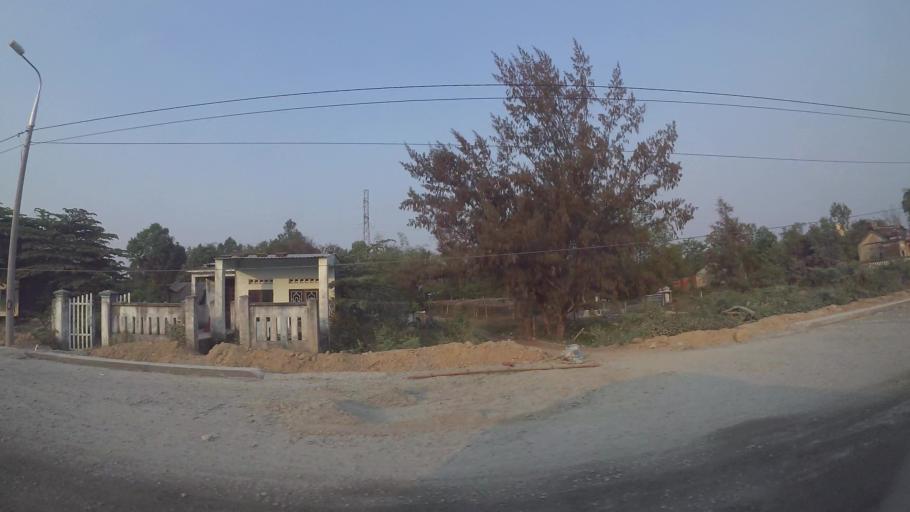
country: VN
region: Da Nang
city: Ngu Hanh Son
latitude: 15.9595
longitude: 108.2327
